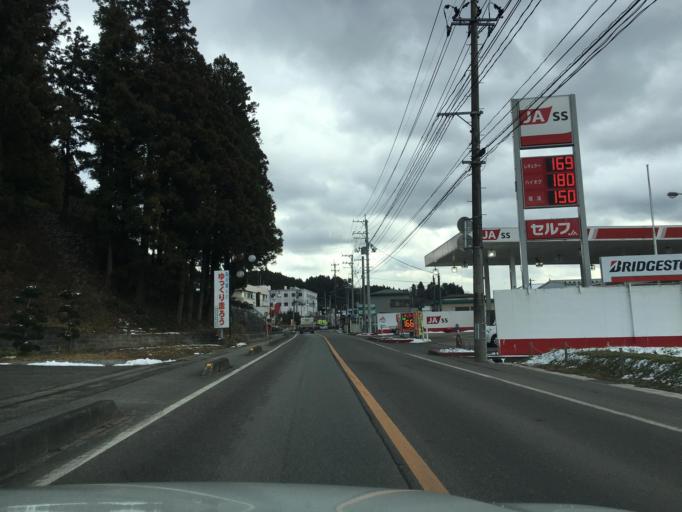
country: JP
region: Fukushima
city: Funehikimachi-funehiki
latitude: 37.2916
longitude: 140.6247
